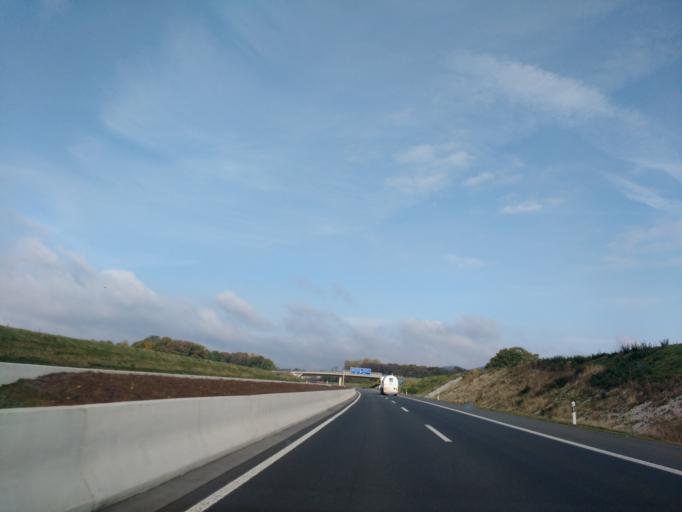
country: DE
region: North Rhine-Westphalia
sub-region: Regierungsbezirk Detmold
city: Steinhagen
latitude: 52.0003
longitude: 8.4411
